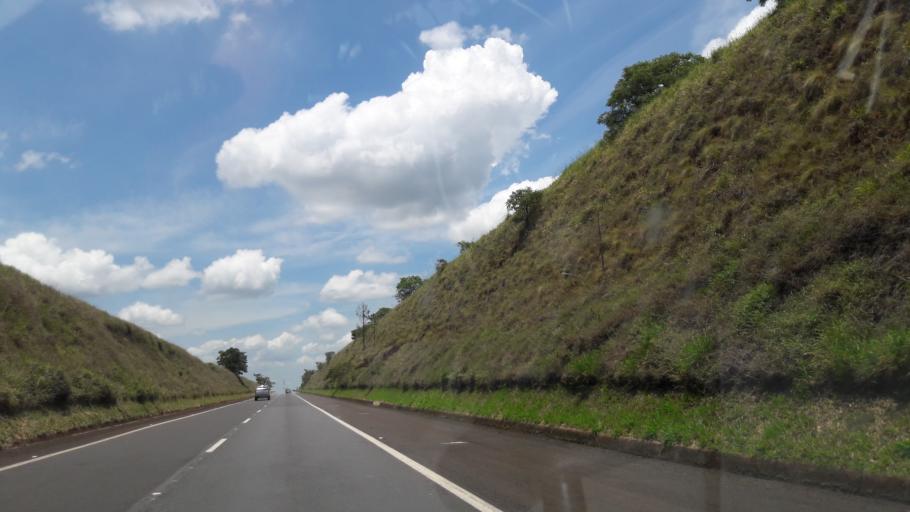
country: BR
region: Sao Paulo
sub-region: Avare
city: Avare
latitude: -22.9552
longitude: -48.8363
